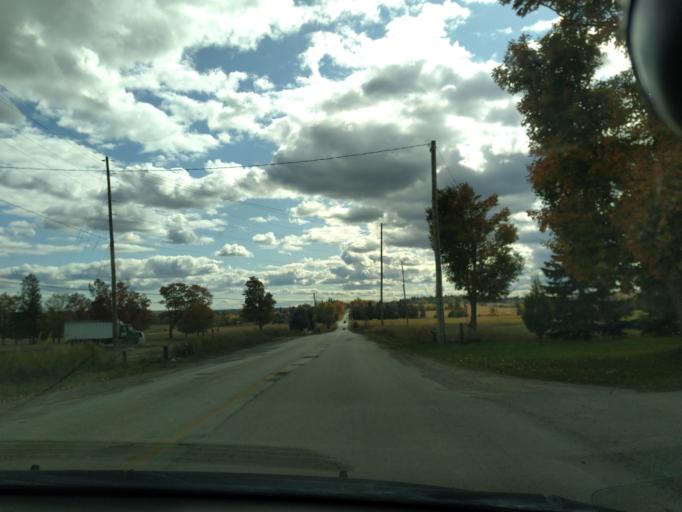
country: CA
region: Ontario
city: Bradford West Gwillimbury
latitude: 44.0860
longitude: -79.5969
